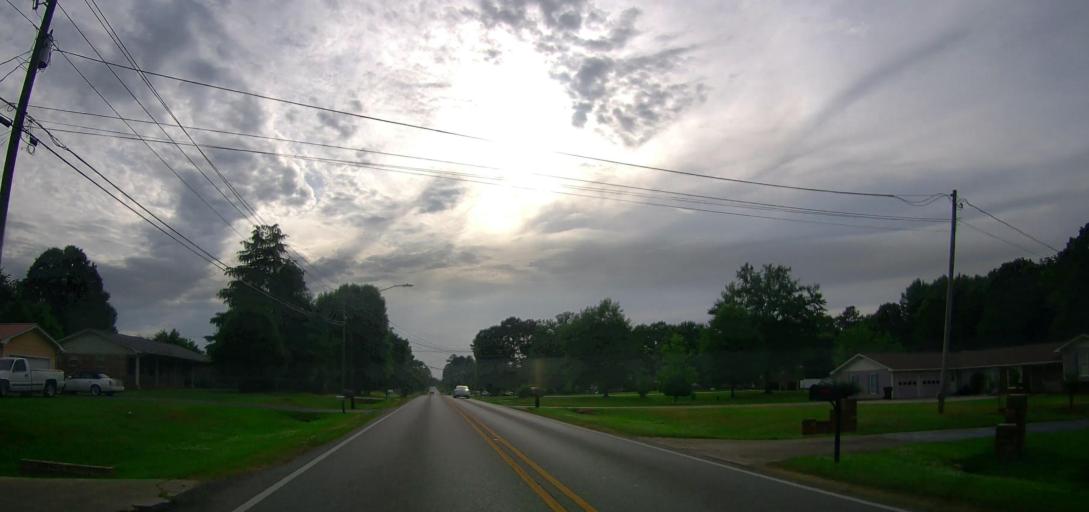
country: US
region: Alabama
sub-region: Calhoun County
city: Oxford
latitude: 33.5855
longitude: -85.7887
